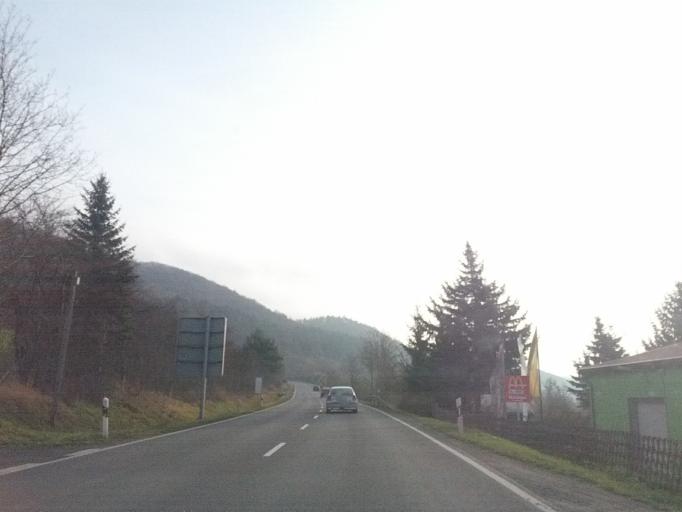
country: DE
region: Thuringia
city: Walldorf
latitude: 50.6166
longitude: 10.3951
